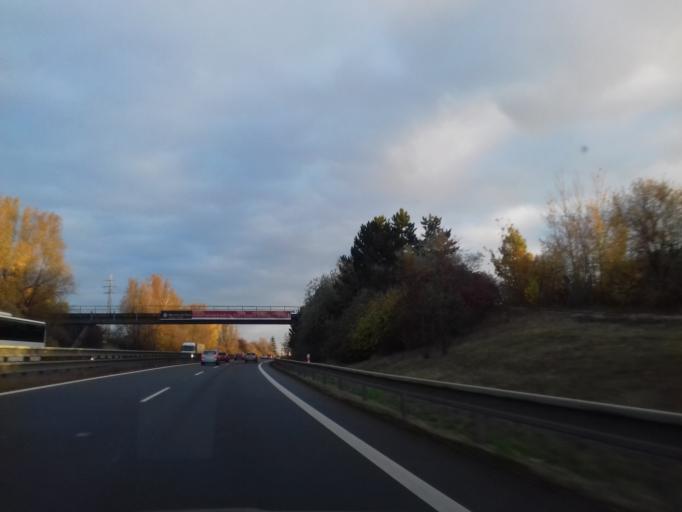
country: CZ
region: Olomoucky
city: Smrzice
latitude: 49.5008
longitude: 17.1414
